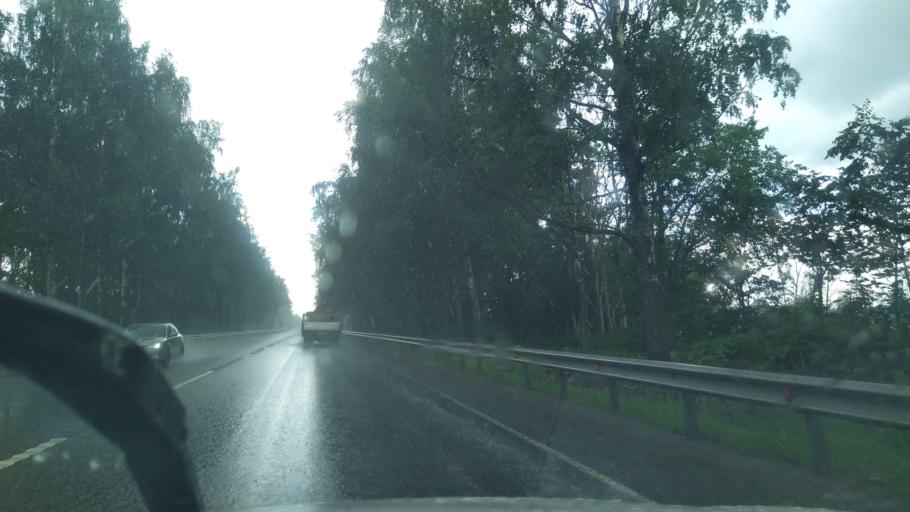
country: RU
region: Leningrad
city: Voyskovitsy
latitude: 59.4731
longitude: 30.0122
